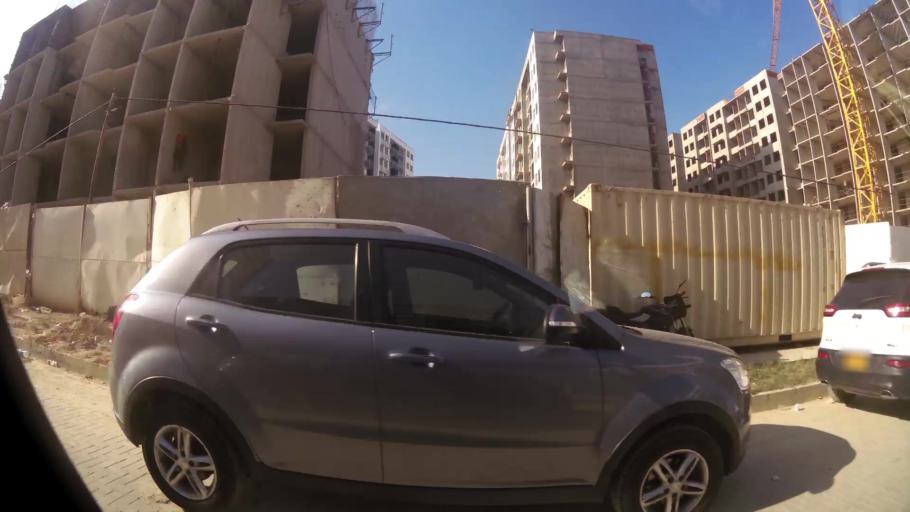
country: CO
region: Atlantico
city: Barranquilla
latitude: 11.0070
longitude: -74.8383
